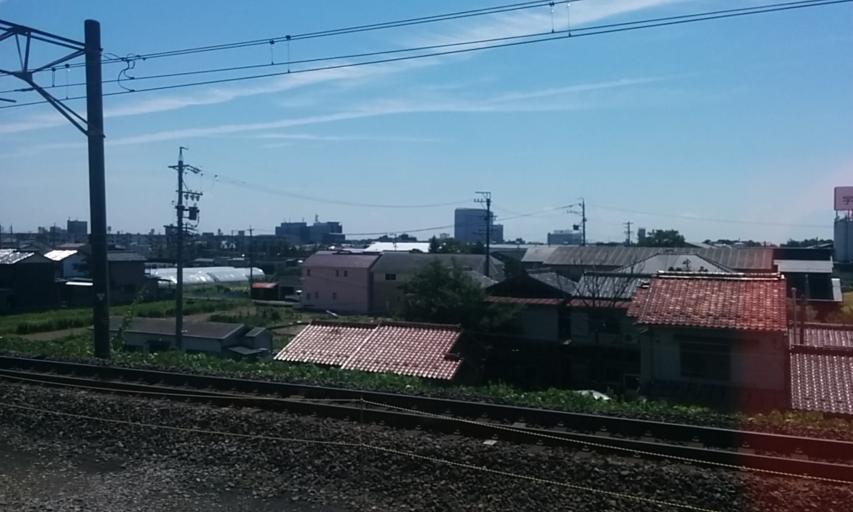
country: JP
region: Gifu
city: Gifu-shi
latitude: 35.4000
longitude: 136.7061
